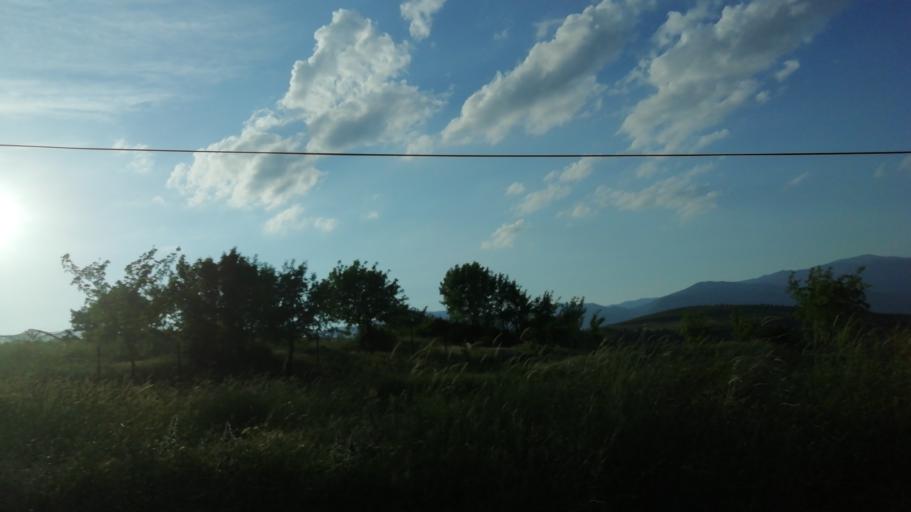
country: TR
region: Karabuk
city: Karabuk
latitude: 41.1310
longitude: 32.6224
